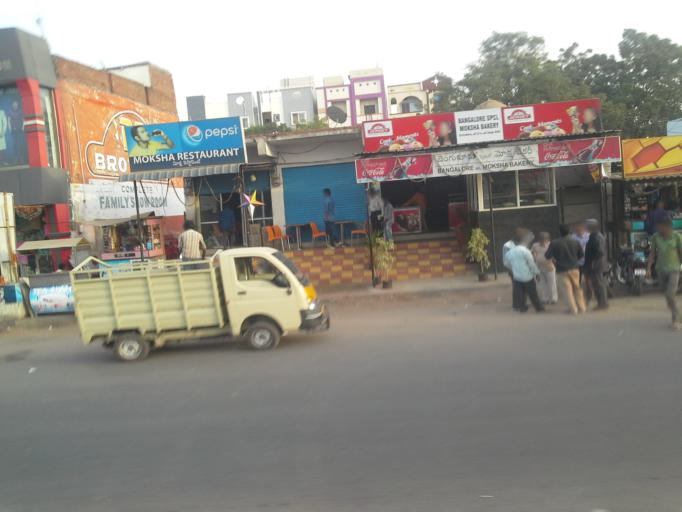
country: IN
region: Telangana
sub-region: Hyderabad
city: Hyderabad
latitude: 17.3542
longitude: 78.3788
